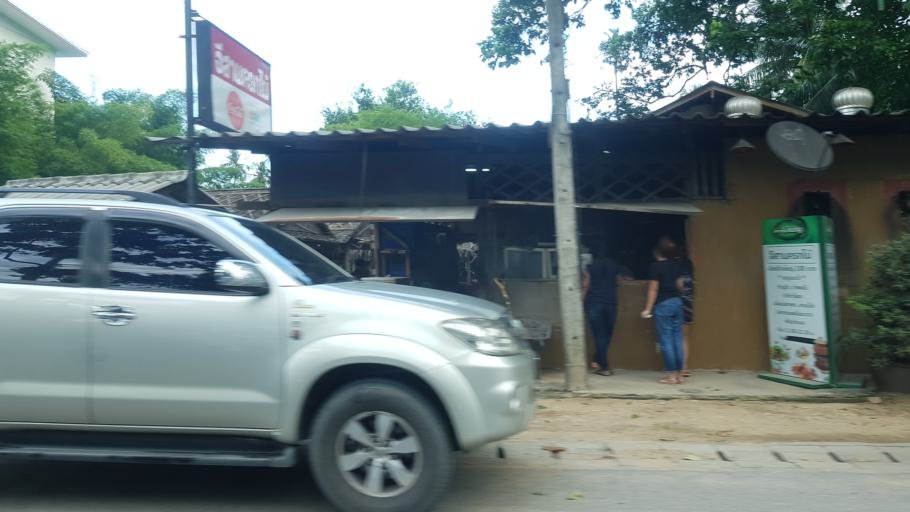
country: TH
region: Surat Thani
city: Ko Samui
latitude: 9.5160
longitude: 100.0500
